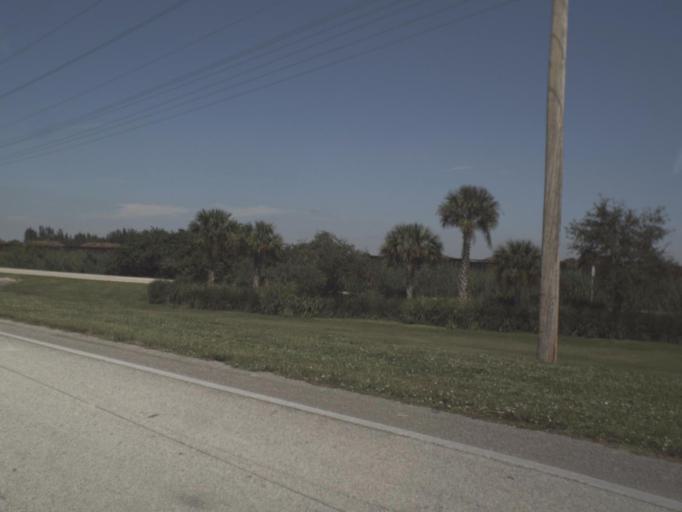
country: US
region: Florida
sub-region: Glades County
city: Moore Haven
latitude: 26.8291
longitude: -81.0828
